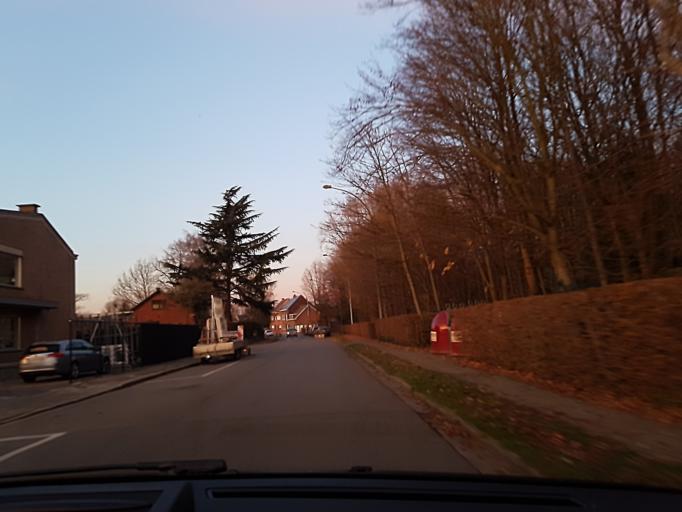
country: BE
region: Flanders
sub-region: Provincie Antwerpen
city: Willebroek
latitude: 51.0552
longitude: 4.3678
